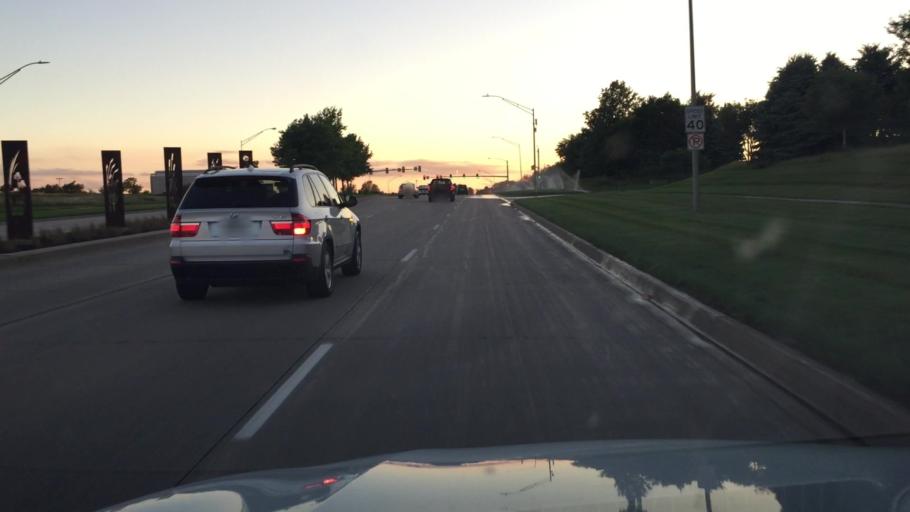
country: US
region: Iowa
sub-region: Polk County
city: Clive
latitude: 41.5618
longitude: -93.8010
